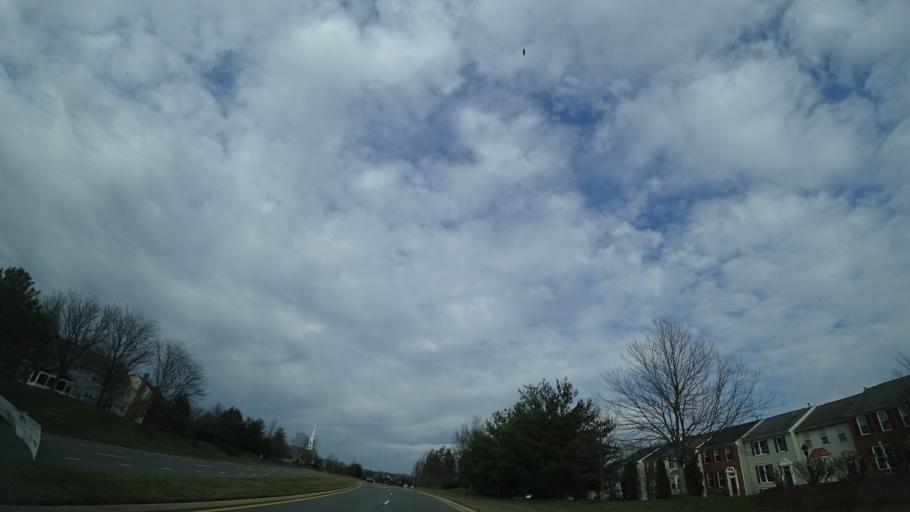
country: US
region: Virginia
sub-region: Loudoun County
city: Ashburn
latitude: 39.0337
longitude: -77.5051
